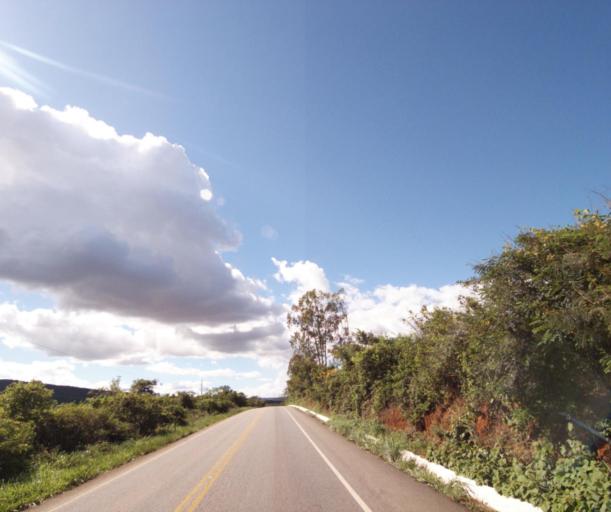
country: BR
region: Bahia
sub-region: Caetite
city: Caetite
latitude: -14.0842
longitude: -42.4510
